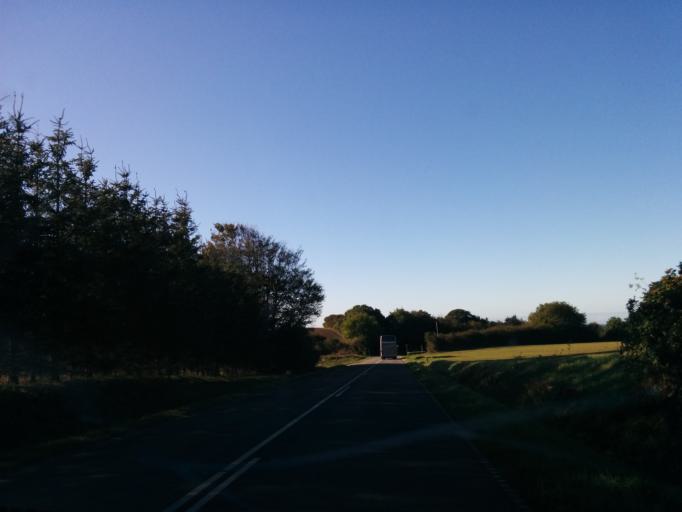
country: DK
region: South Denmark
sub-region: Kolding Kommune
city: Sonder Bjert
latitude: 55.4132
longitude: 9.5600
